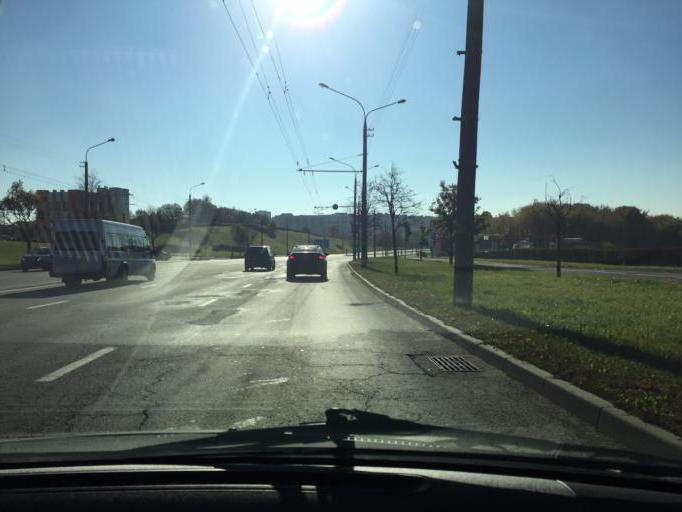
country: BY
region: Minsk
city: Syenitsa
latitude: 53.8603
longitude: 27.5369
